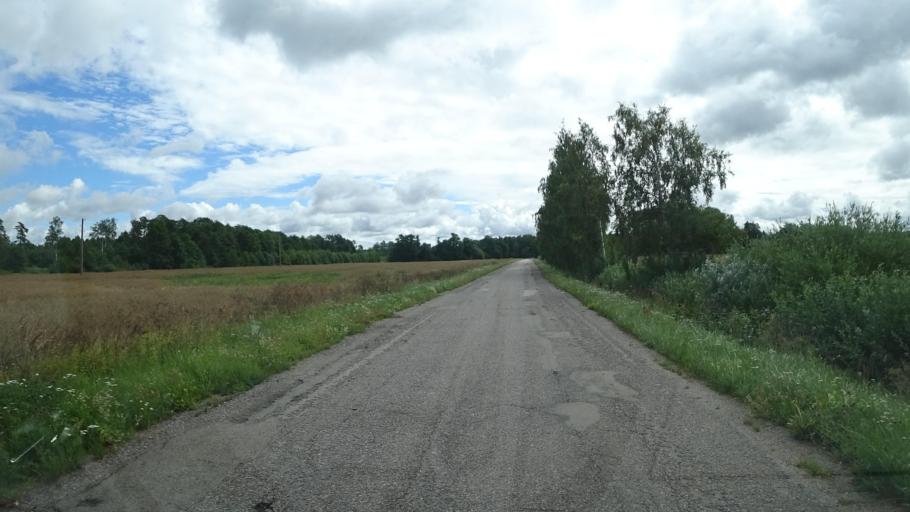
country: LV
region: Liepaja
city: Vec-Liepaja
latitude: 56.6592
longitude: 21.0840
